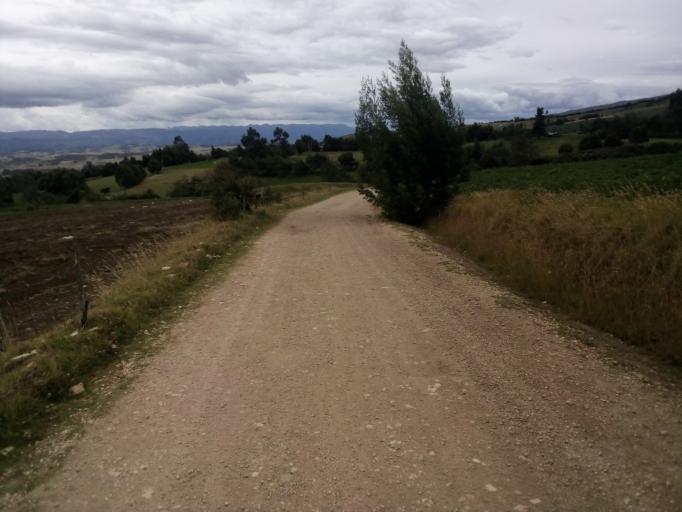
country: CO
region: Boyaca
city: Toca
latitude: 5.5797
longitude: -73.1454
